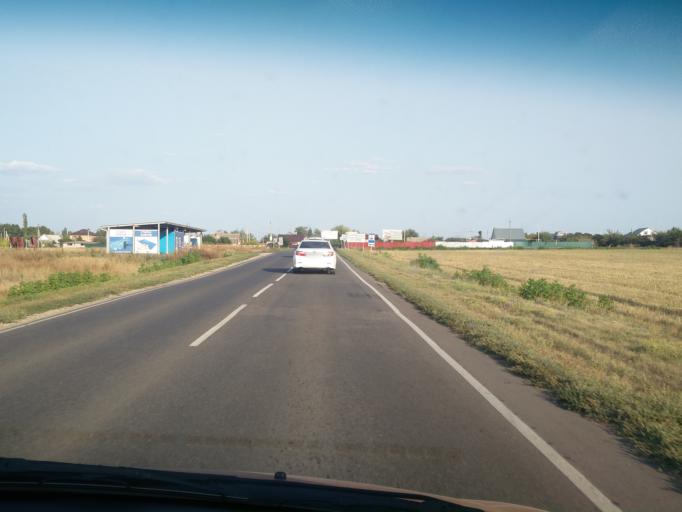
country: RU
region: Voronezj
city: Ramon'
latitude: 51.9345
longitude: 39.3439
